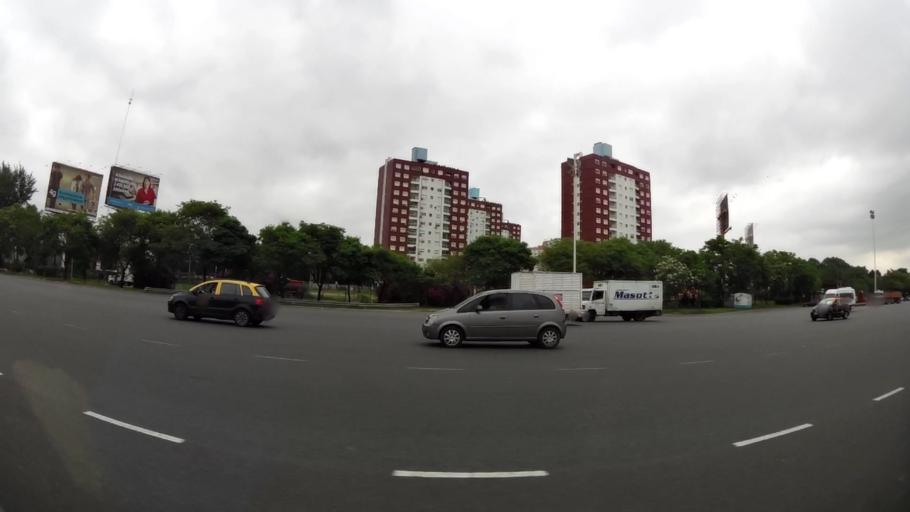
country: AR
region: Buenos Aires F.D.
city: Villa Lugano
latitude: -34.7006
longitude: -58.4970
